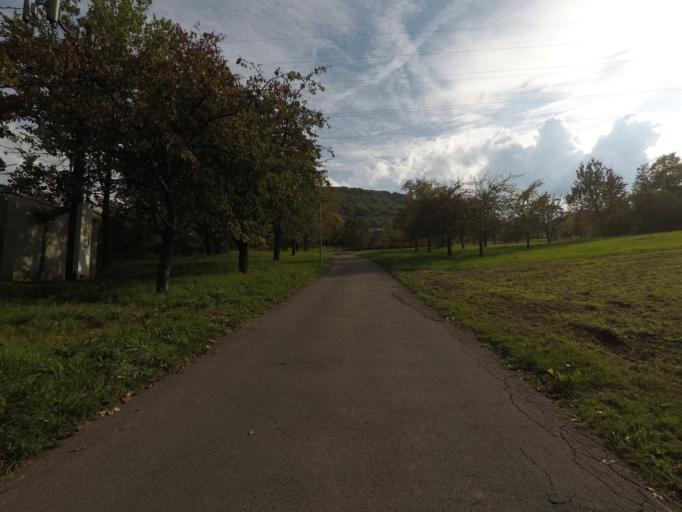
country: DE
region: Baden-Wuerttemberg
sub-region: Tuebingen Region
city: Pfullingen
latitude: 48.4536
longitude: 9.2214
